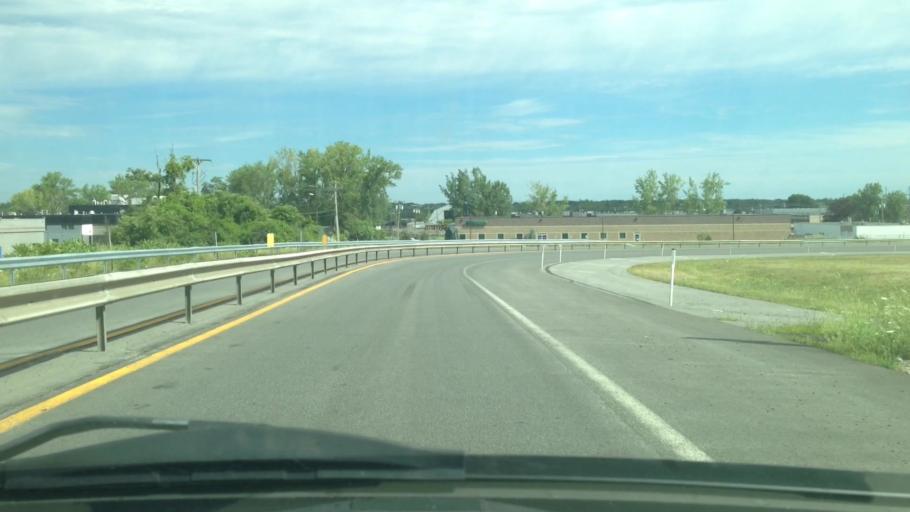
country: US
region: New York
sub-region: Onondaga County
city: East Syracuse
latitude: 43.0935
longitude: -76.0899
